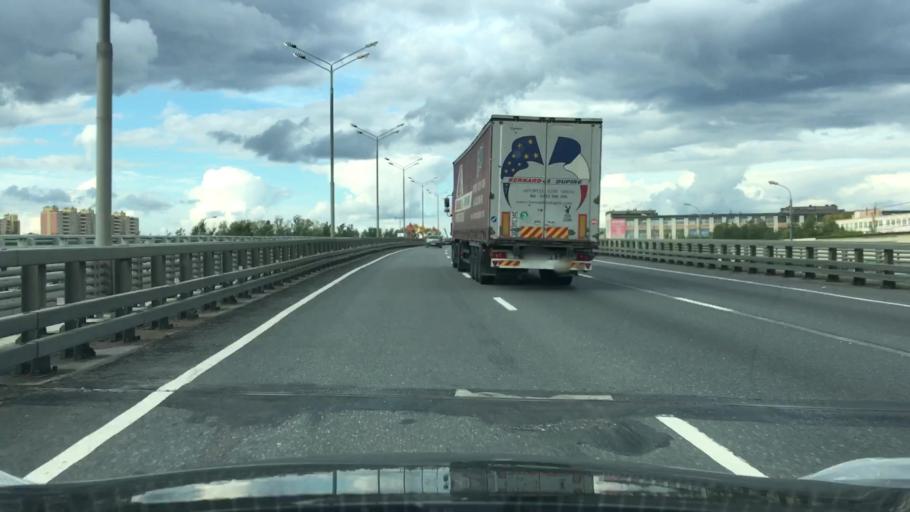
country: RU
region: Tverskaya
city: Tver
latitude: 56.8404
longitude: 35.7934
